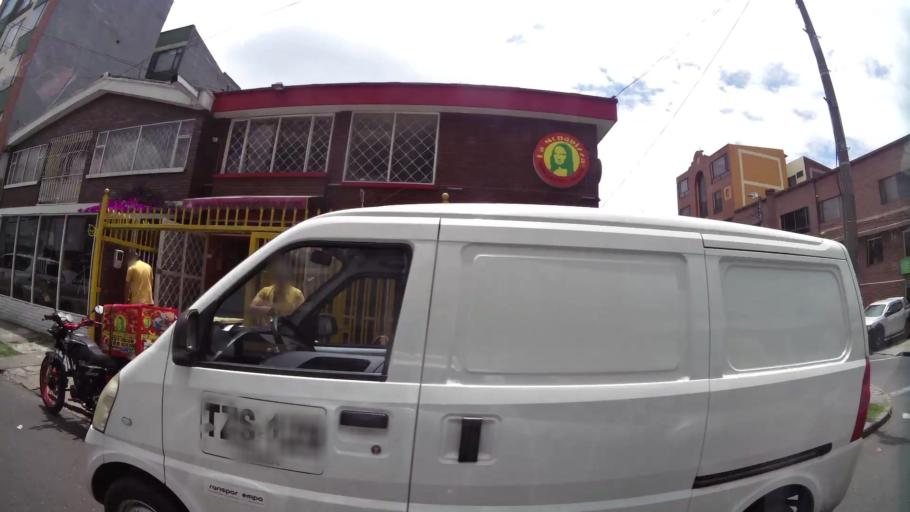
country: CO
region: Bogota D.C.
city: Bogota
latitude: 4.6322
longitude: -74.0945
